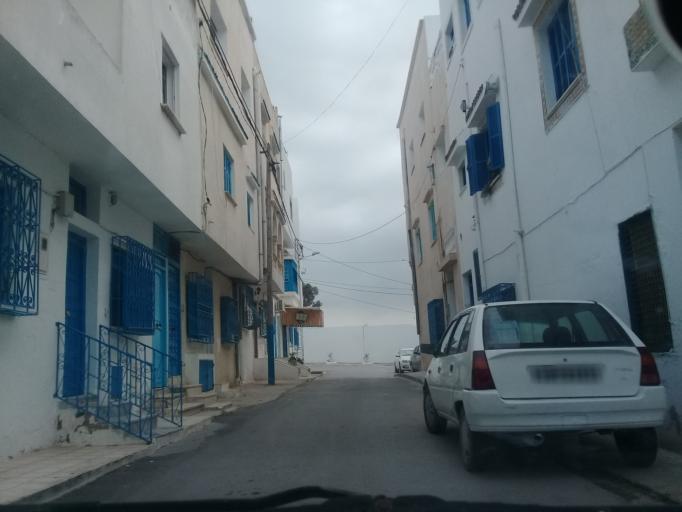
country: TN
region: Tunis
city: Sidi Bou Said
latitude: 36.8715
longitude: 10.3373
